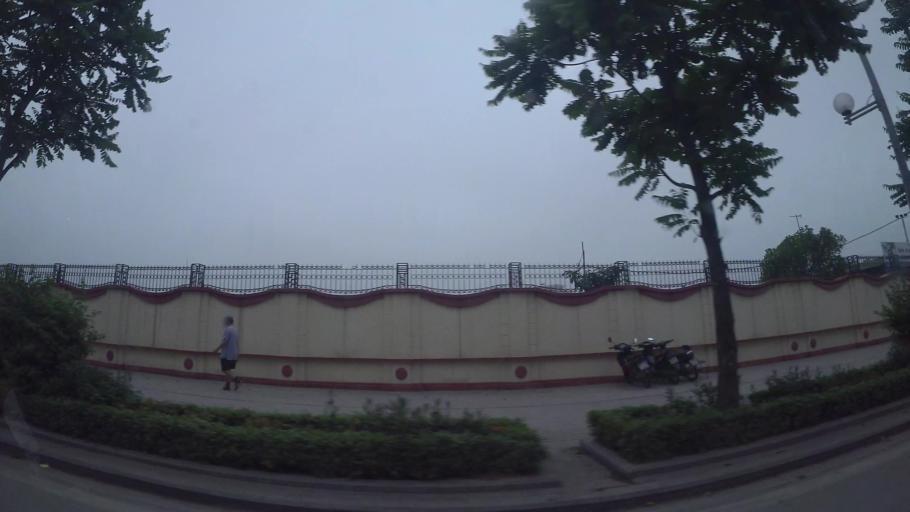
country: VN
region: Ha Noi
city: Hai BaTrung
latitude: 20.9944
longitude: 105.8311
